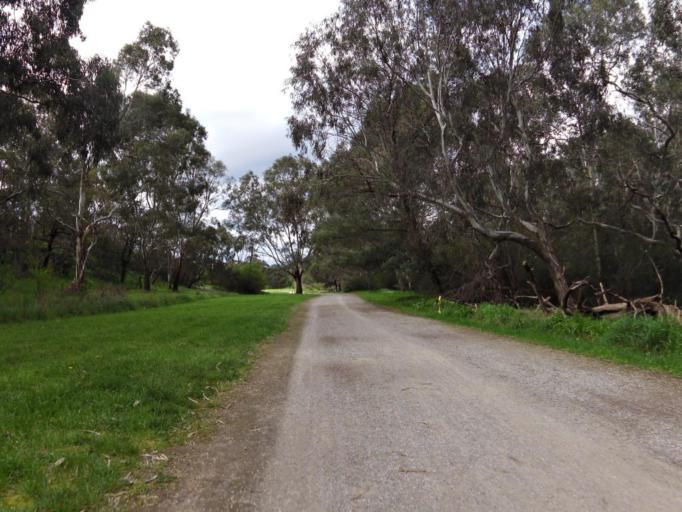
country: AU
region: Victoria
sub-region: Manningham
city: Bulleen
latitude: -37.7716
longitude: 145.0697
